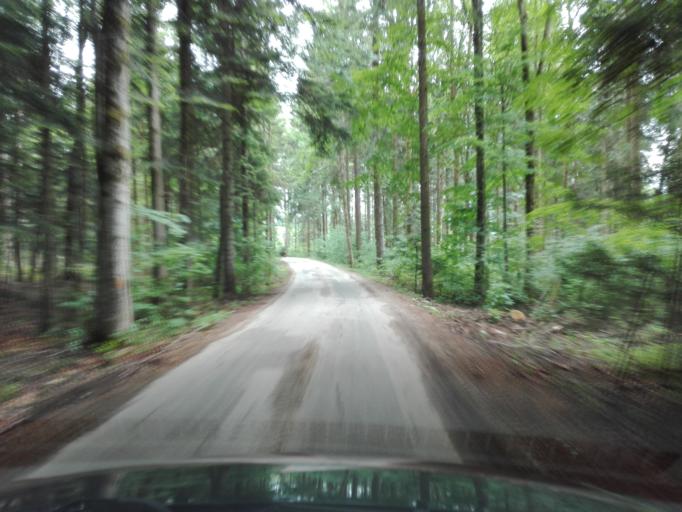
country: AT
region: Upper Austria
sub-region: Politischer Bezirk Gmunden
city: Scharnstein
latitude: 47.9323
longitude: 13.9475
